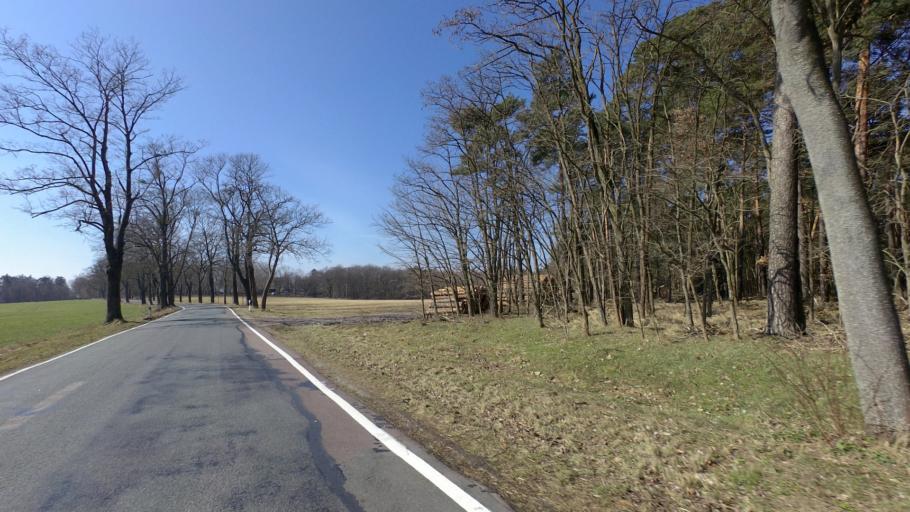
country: DE
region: Saxony-Anhalt
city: Nudersdorf
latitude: 51.9118
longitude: 12.5225
